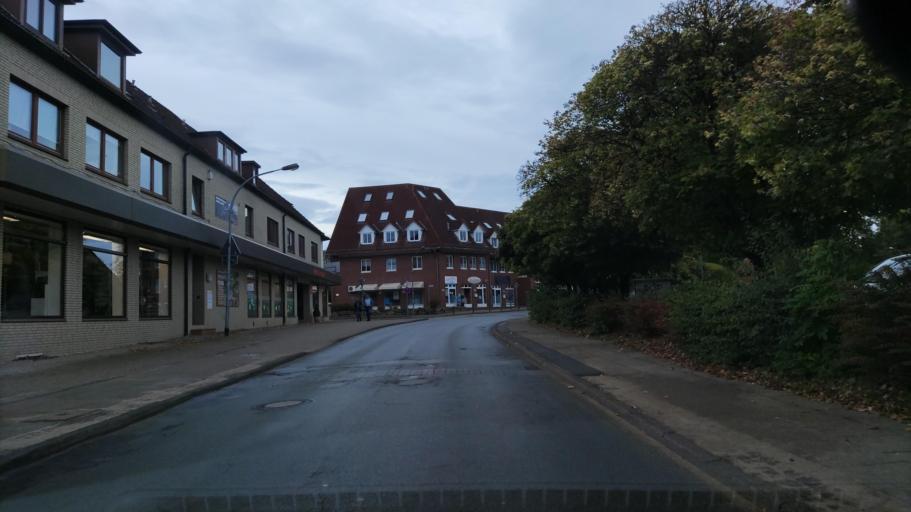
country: DE
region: Schleswig-Holstein
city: Trittau
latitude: 53.6128
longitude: 10.4031
